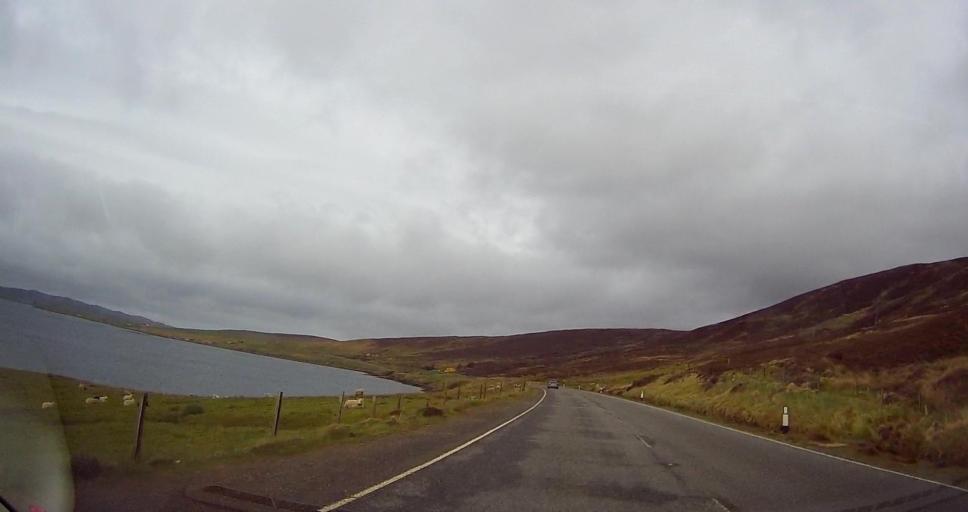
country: GB
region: Scotland
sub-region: Shetland Islands
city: Lerwick
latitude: 60.3652
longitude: -1.2888
